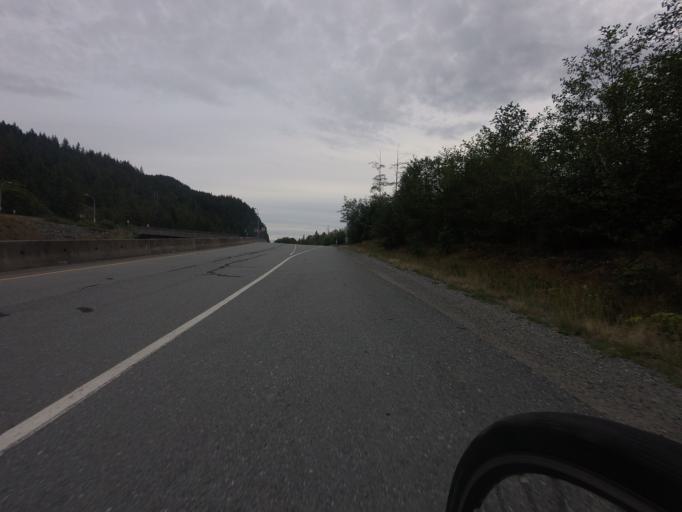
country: CA
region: British Columbia
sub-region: Greater Vancouver Regional District
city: Lions Bay
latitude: 49.5460
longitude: -123.2414
